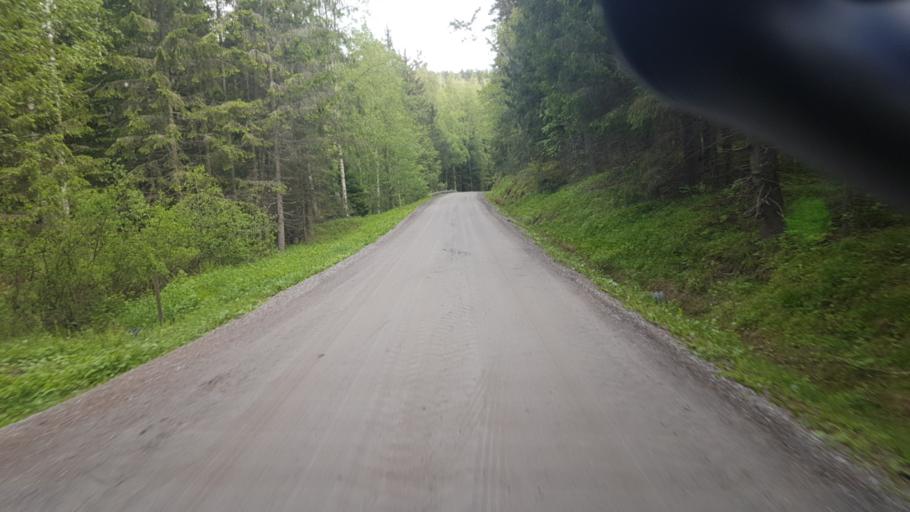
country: NO
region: Ostfold
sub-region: Romskog
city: Romskog
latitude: 59.6994
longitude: 11.9461
